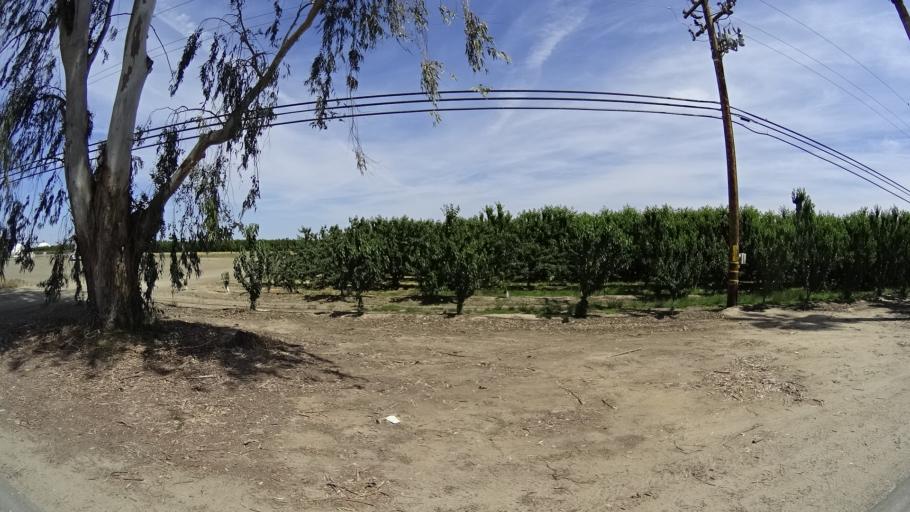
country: US
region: California
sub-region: Kings County
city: Home Garden
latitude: 36.3280
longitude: -119.5982
